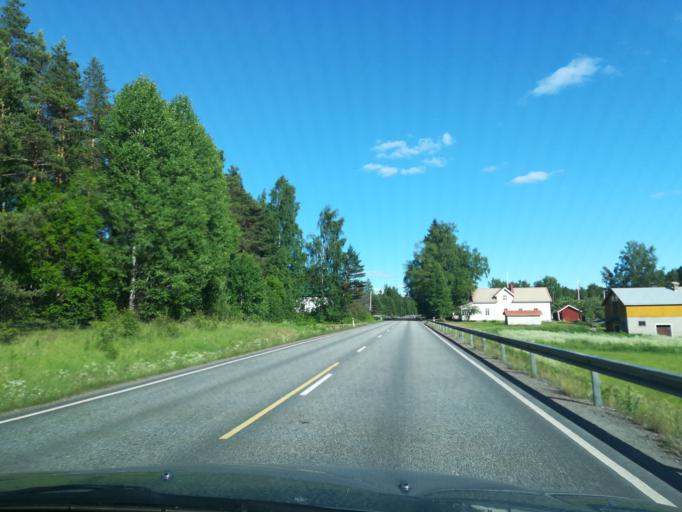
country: FI
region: South Karelia
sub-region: Imatra
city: Ruokolahti
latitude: 61.3728
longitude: 28.6654
